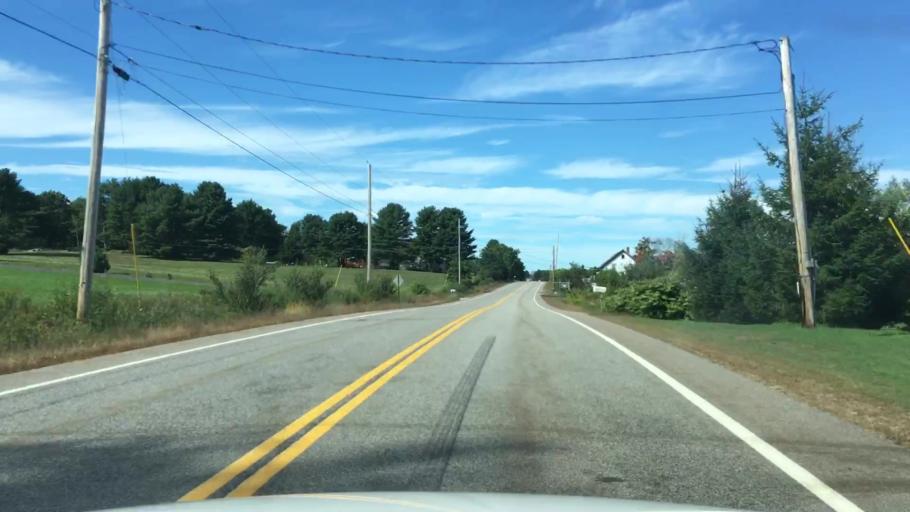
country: US
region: Maine
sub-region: Cumberland County
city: Westbrook
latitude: 43.6606
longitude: -70.4034
